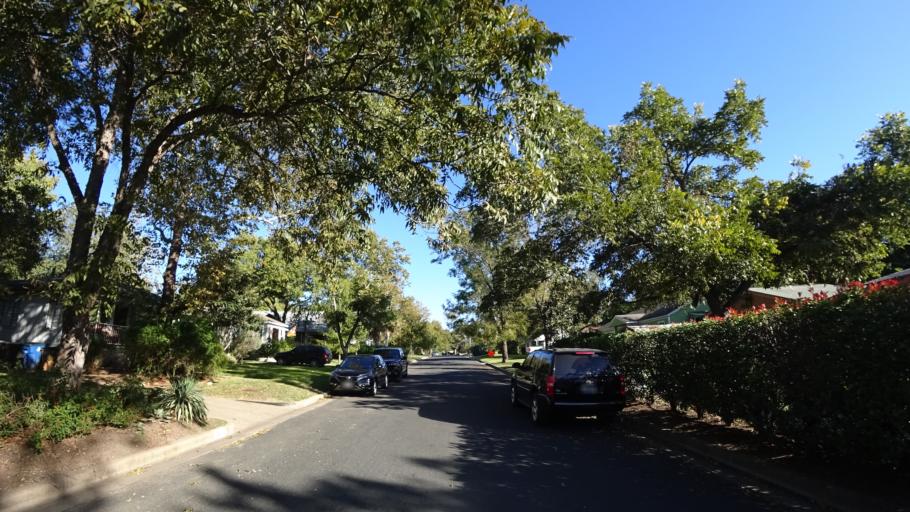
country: US
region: Texas
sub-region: Travis County
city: Austin
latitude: 30.3069
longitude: -97.7567
